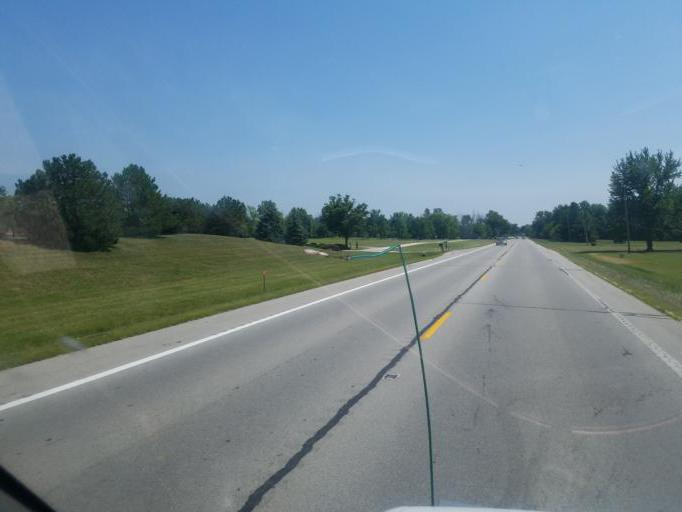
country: US
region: Ohio
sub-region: Mercer County
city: Celina
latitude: 40.5143
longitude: -84.5775
